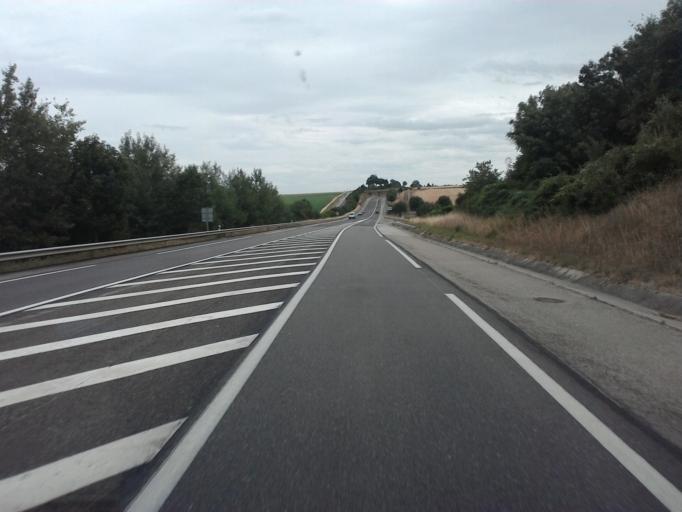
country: FR
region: Lorraine
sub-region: Departement de Meurthe-et-Moselle
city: Chaligny
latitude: 48.5813
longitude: 6.0182
